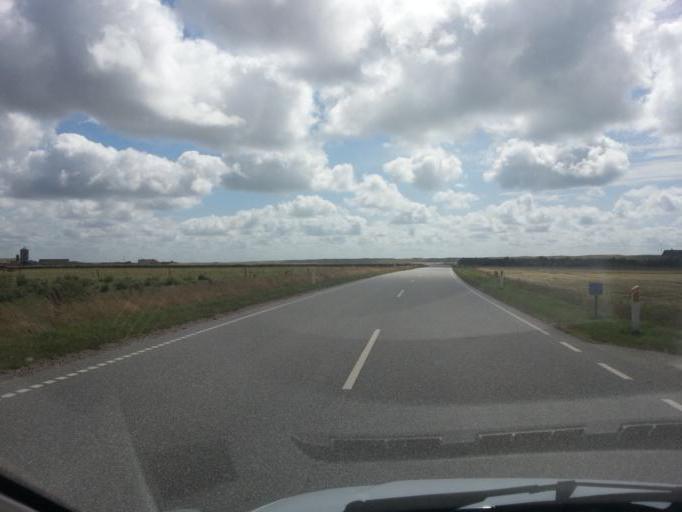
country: DK
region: Central Jutland
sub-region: Lemvig Kommune
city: Harboore
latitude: 56.4626
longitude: 8.1339
